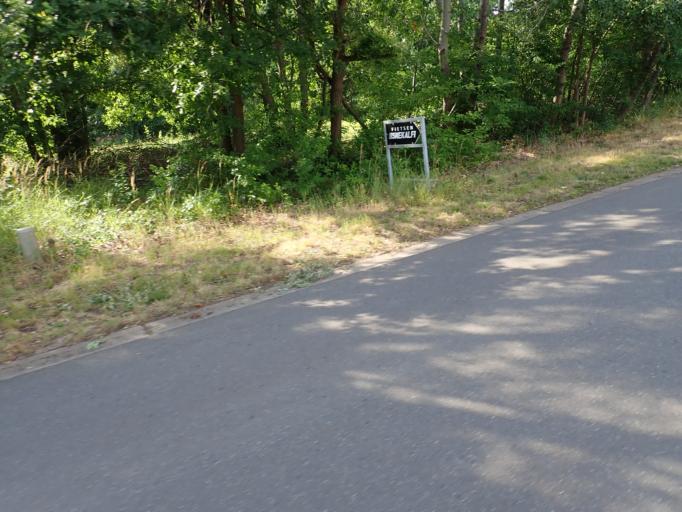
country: BE
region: Flanders
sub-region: Provincie Vlaams-Brabant
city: Keerbergen
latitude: 51.0129
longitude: 4.6316
